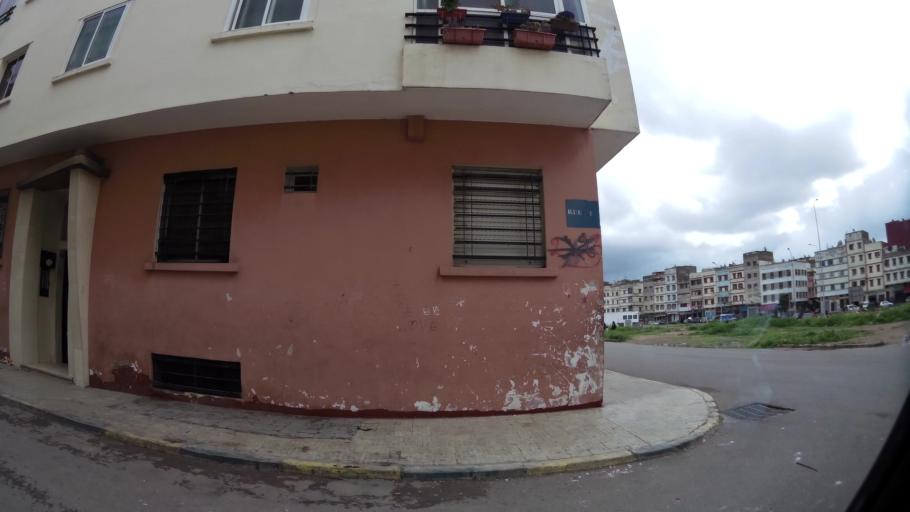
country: MA
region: Grand Casablanca
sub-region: Casablanca
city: Casablanca
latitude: 33.5666
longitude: -7.5936
